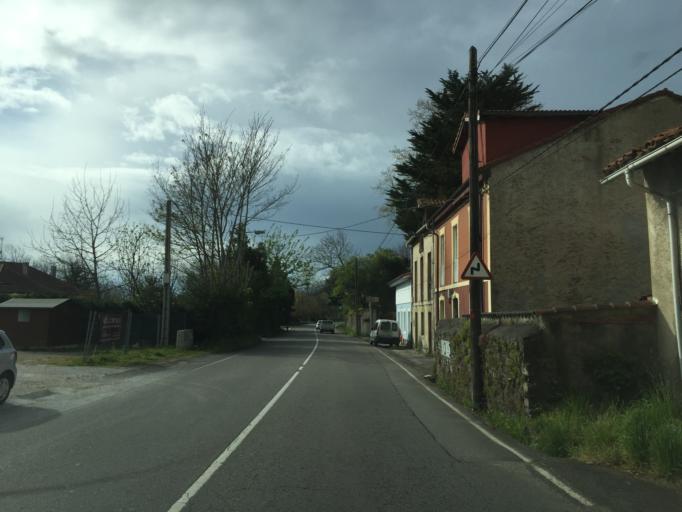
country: ES
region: Asturias
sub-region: Province of Asturias
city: Gijon
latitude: 43.5166
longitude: -5.6048
